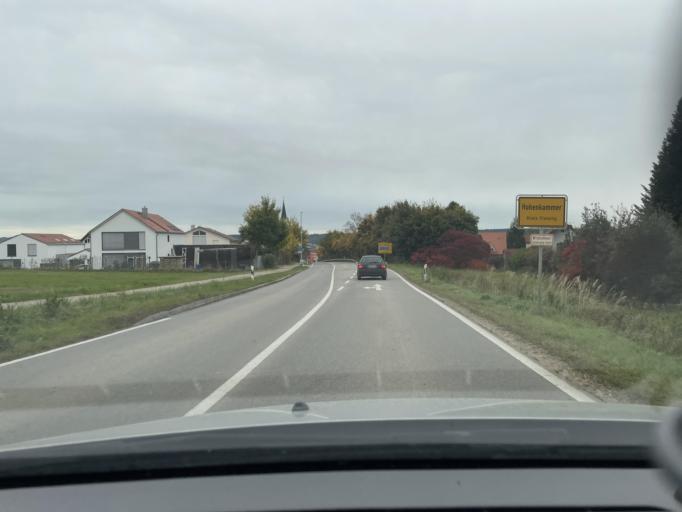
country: DE
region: Bavaria
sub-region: Upper Bavaria
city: Hohenkammer
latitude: 48.4209
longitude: 11.5290
